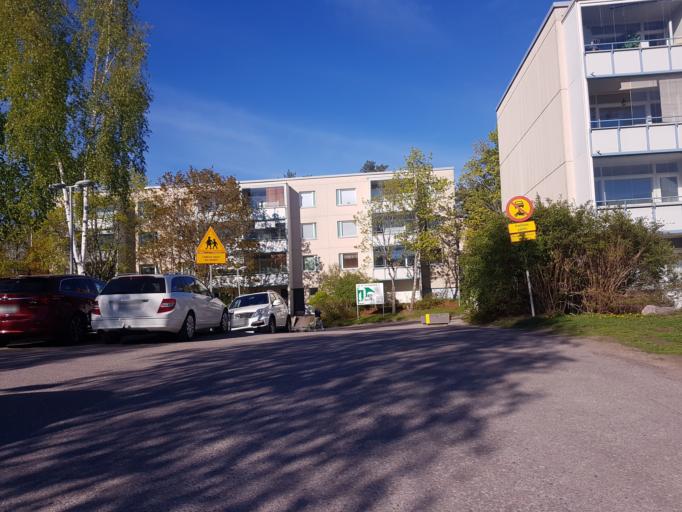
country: FI
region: Uusimaa
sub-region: Helsinki
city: Vantaa
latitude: 60.2334
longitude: 24.9975
